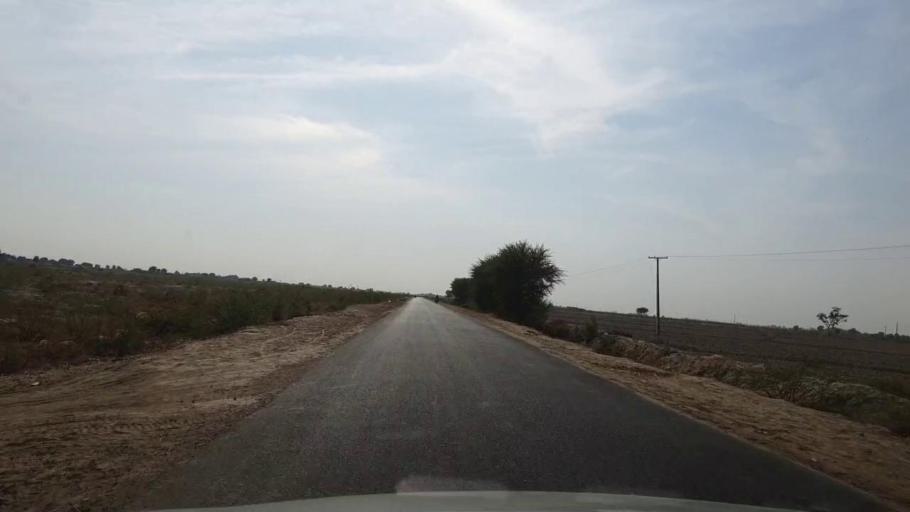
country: PK
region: Sindh
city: Kunri
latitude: 25.1623
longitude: 69.5077
